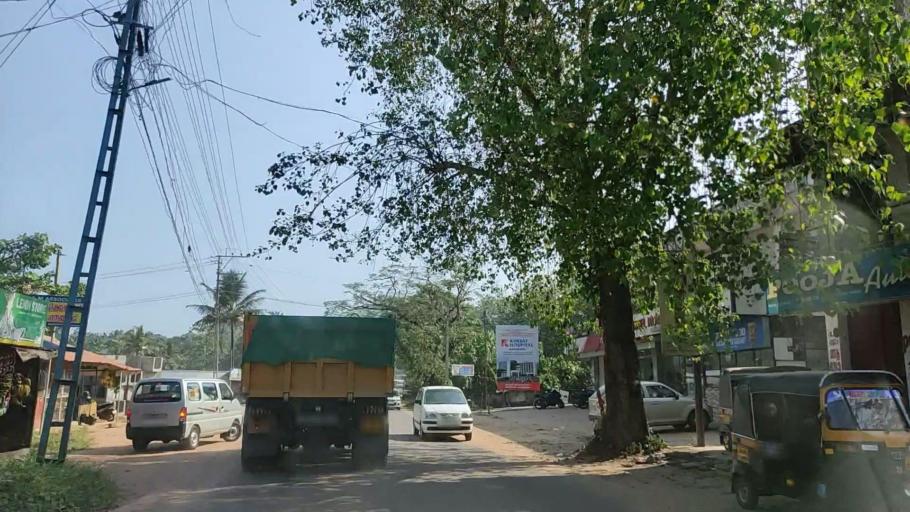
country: IN
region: Kerala
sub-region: Kollam
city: Punalur
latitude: 8.9253
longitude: 76.9022
